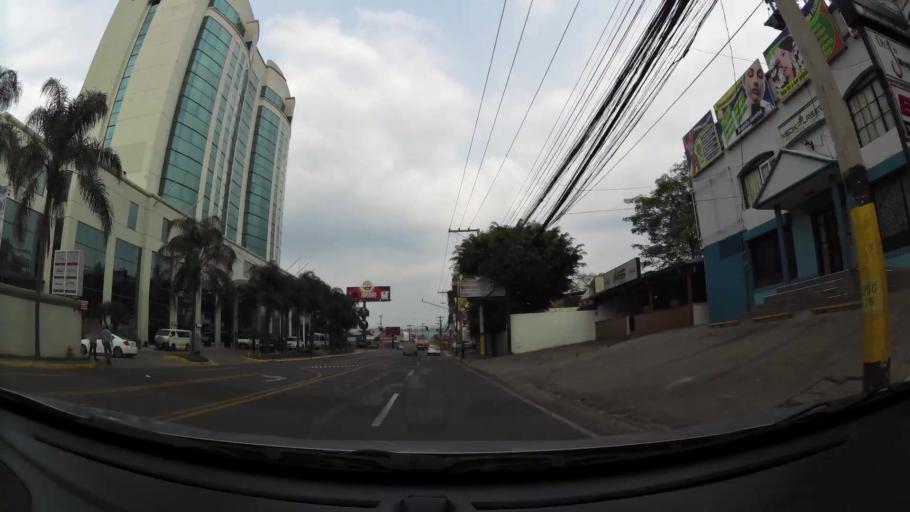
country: HN
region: Francisco Morazan
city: Tegucigalpa
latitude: 14.0894
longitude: -87.1895
